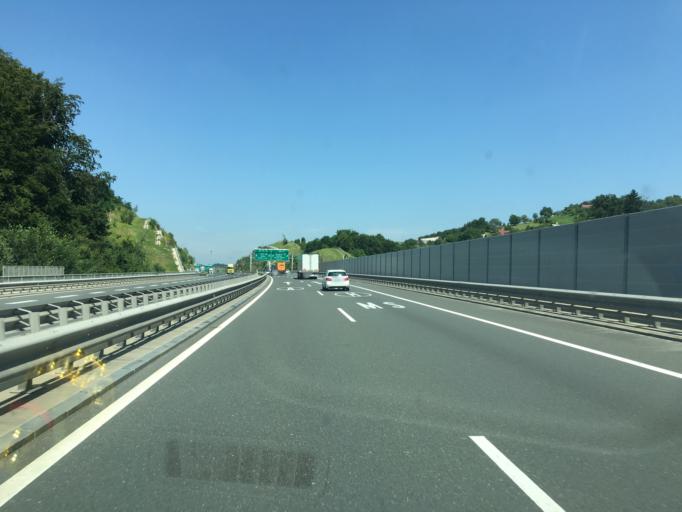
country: SI
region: Pesnica
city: Pesnica pri Mariboru
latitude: 46.5770
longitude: 15.6898
